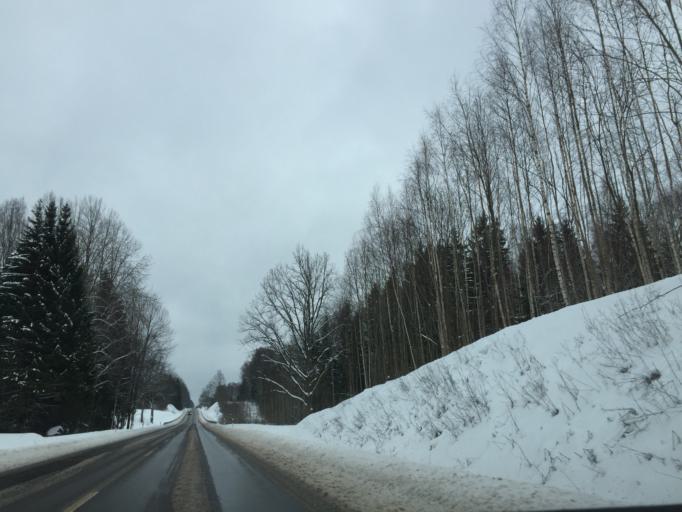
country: LV
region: Ligatne
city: Ligatne
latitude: 57.1332
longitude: 25.0854
